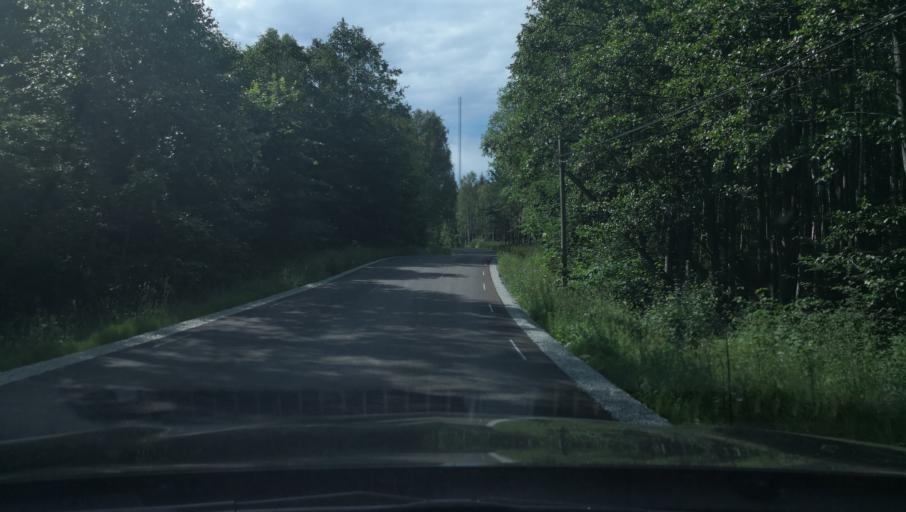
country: SE
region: Vaestmanland
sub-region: Norbergs Kommun
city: Norberg
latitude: 59.9641
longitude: 15.9937
